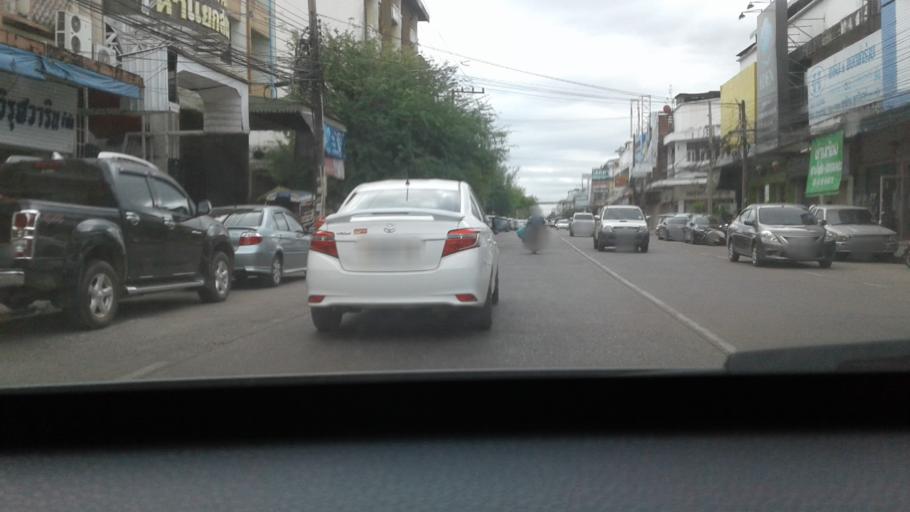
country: TH
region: Changwat Udon Thani
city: Udon Thani
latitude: 17.4048
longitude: 102.7914
